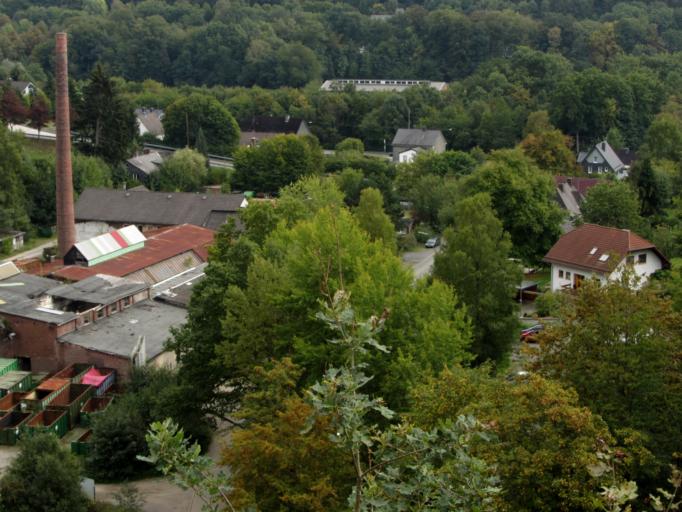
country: DE
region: North Rhine-Westphalia
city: Hilchenbach
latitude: 50.9812
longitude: 8.0821
